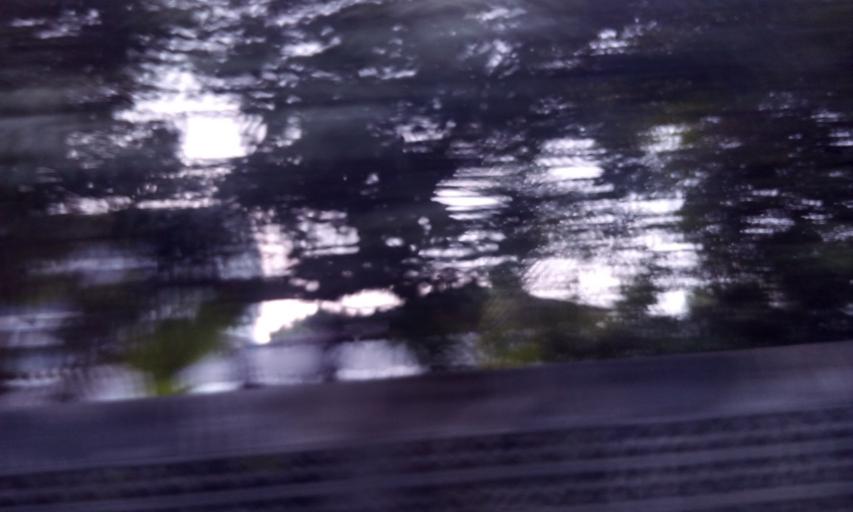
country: TH
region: Bangkok
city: Nong Chok
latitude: 13.8536
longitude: 100.8861
